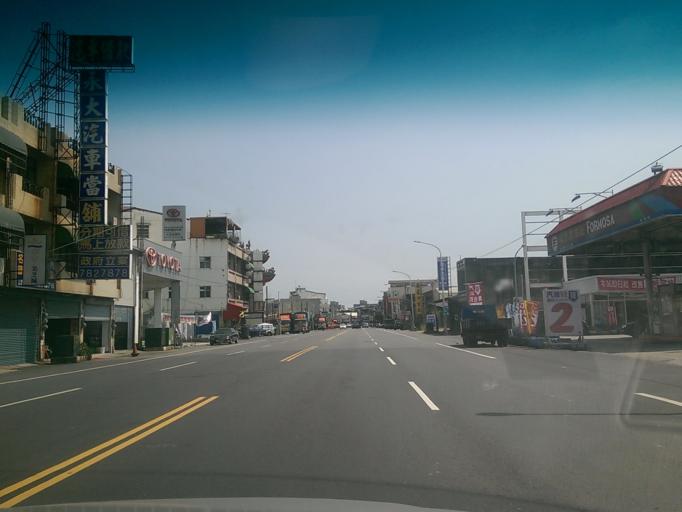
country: TW
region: Taiwan
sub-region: Chiayi
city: Taibao
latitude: 23.5824
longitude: 120.2989
